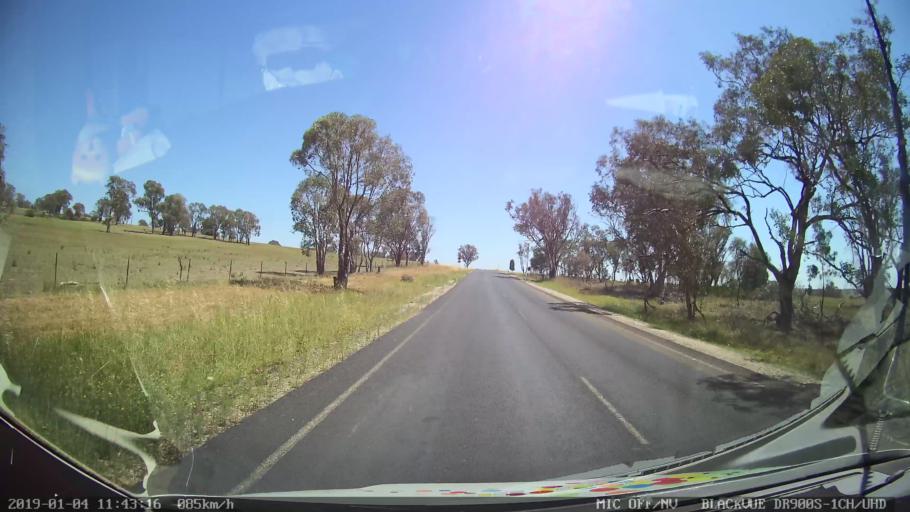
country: AU
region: New South Wales
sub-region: Cabonne
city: Molong
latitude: -32.9711
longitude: 148.7842
